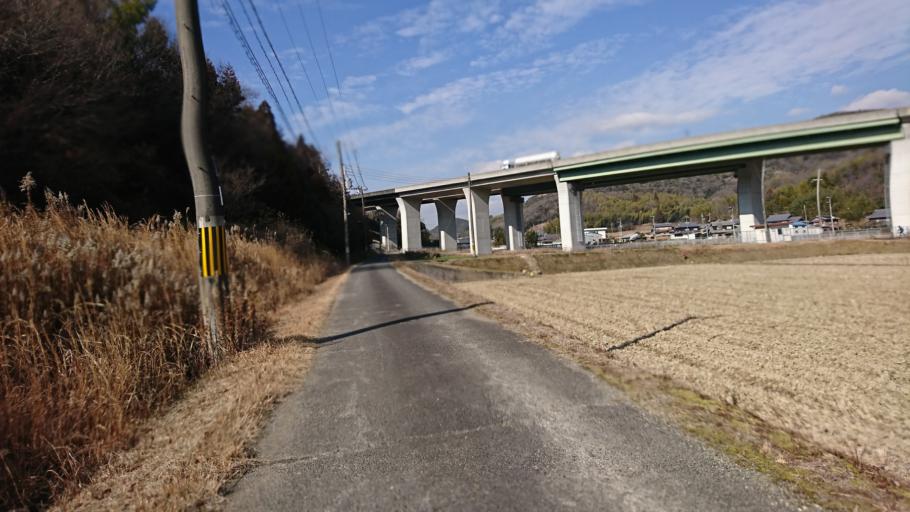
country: JP
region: Hyogo
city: Ono
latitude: 34.8382
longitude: 134.8640
